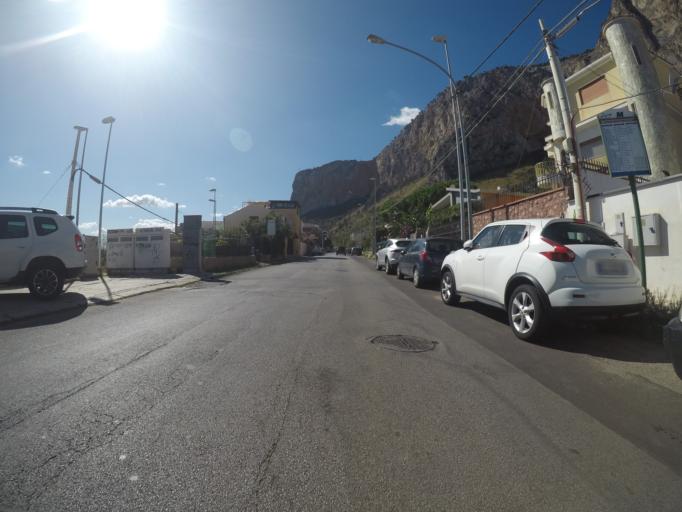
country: IT
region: Sicily
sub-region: Palermo
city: Palermo
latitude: 38.1685
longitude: 13.3665
